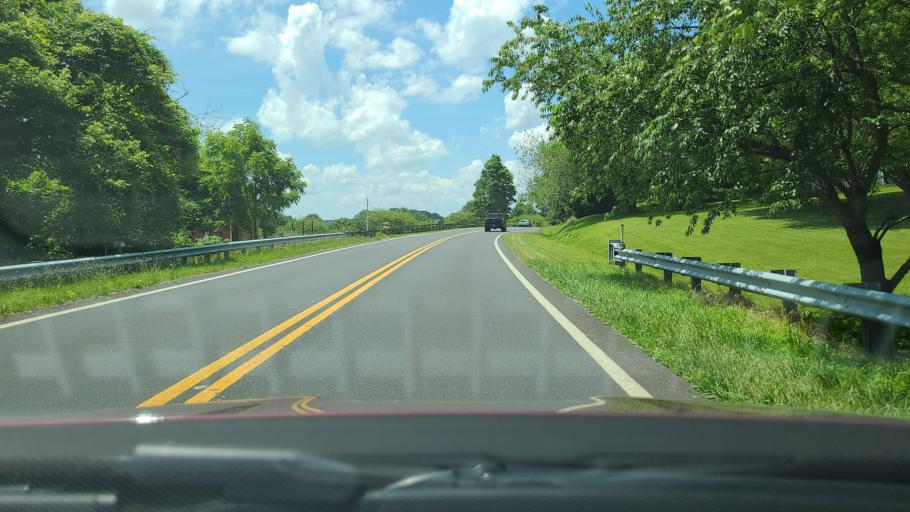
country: US
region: Maryland
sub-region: Carroll County
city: Westminster
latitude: 39.5381
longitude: -76.9995
